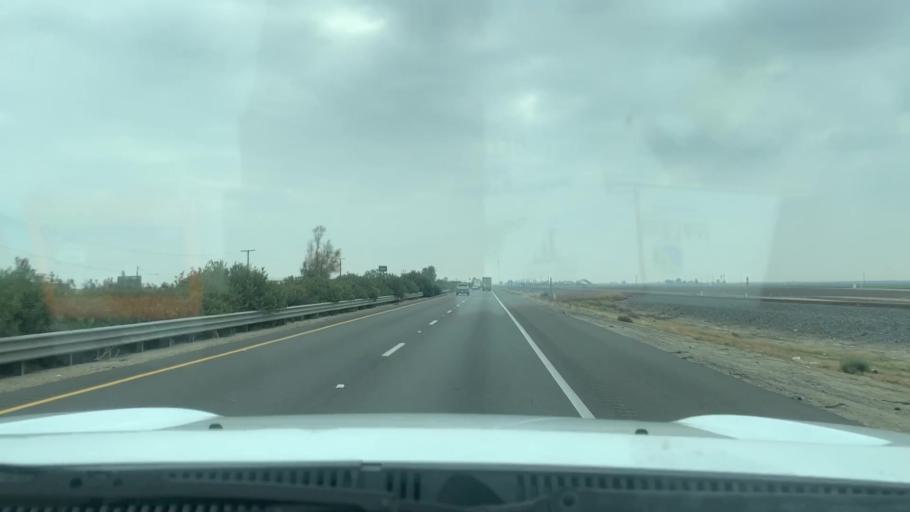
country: US
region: California
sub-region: Tulare County
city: Tipton
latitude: 36.0876
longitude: -119.3209
